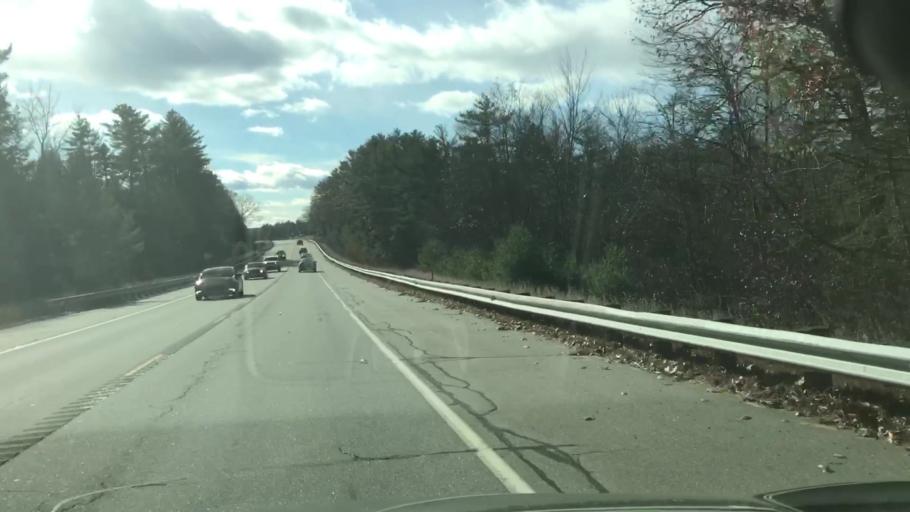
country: US
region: New Hampshire
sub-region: Merrimack County
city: Pittsfield
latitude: 43.2893
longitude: -71.3571
